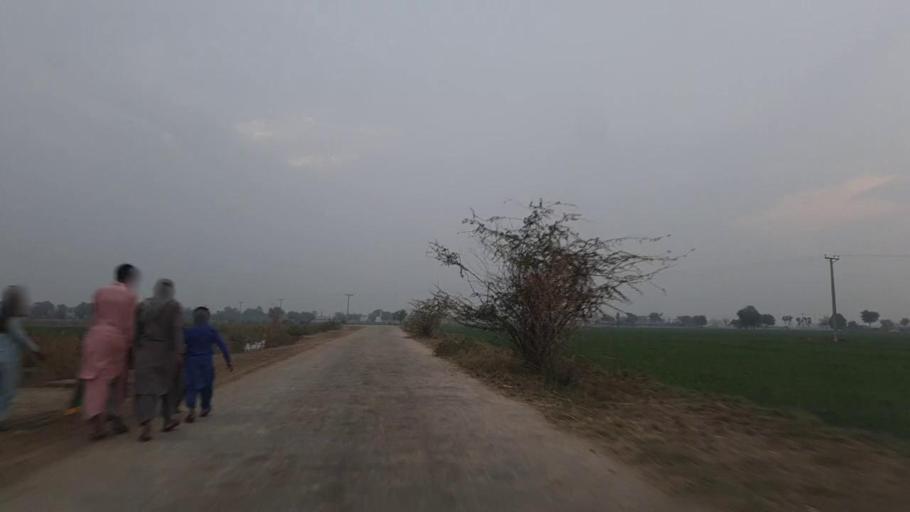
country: PK
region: Sindh
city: Jam Sahib
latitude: 26.3404
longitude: 68.5648
